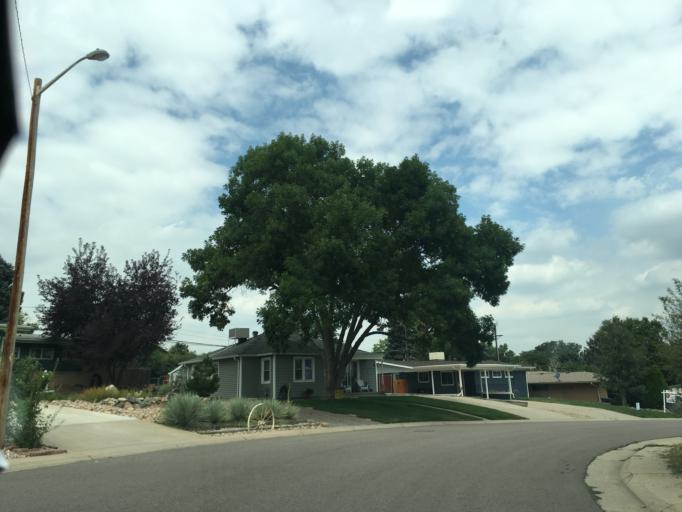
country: US
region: Colorado
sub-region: Arapahoe County
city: Sheridan
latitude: 39.6669
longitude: -105.0375
